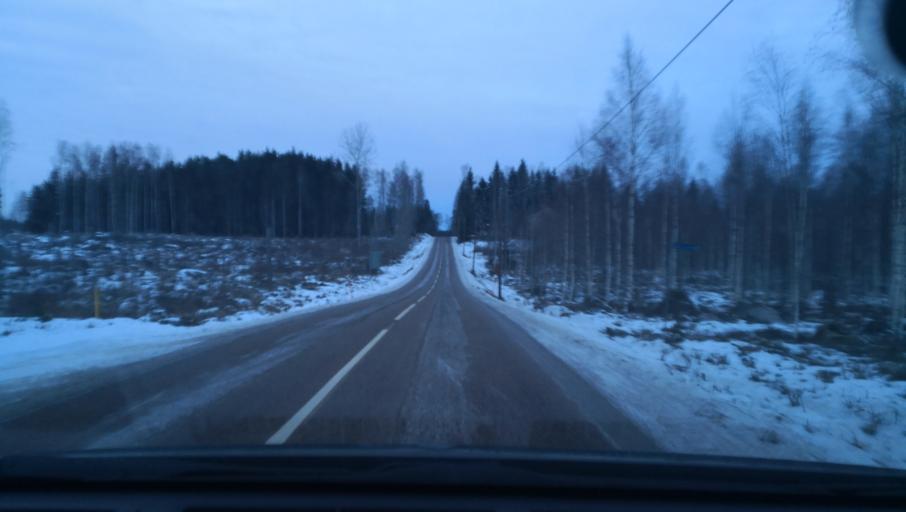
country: SE
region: Dalarna
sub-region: Avesta Kommun
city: Horndal
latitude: 60.1925
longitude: 16.4671
